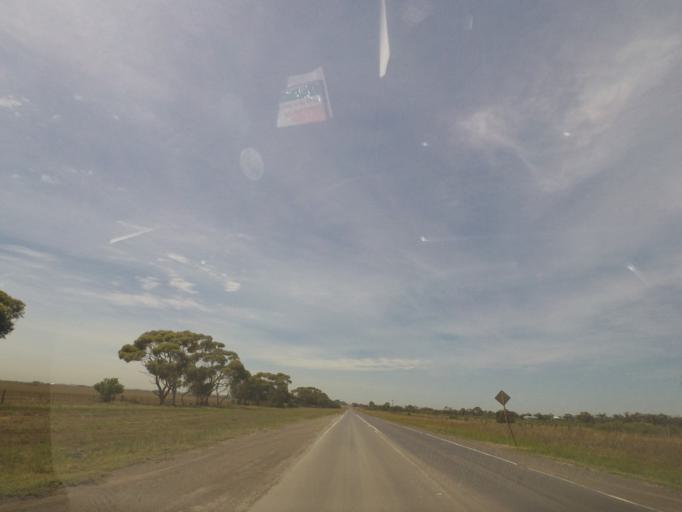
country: AU
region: Victoria
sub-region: Wyndham
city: Wyndham Vale
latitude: -37.8464
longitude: 144.5759
